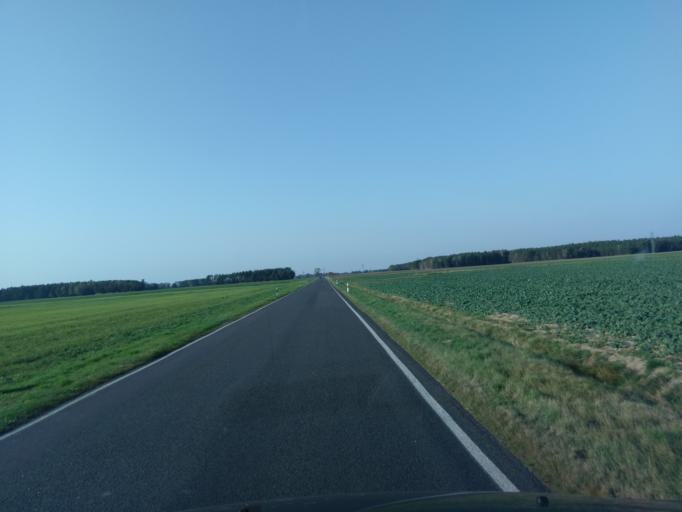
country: DE
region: Brandenburg
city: Falkenberg
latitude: 51.5469
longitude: 13.2753
